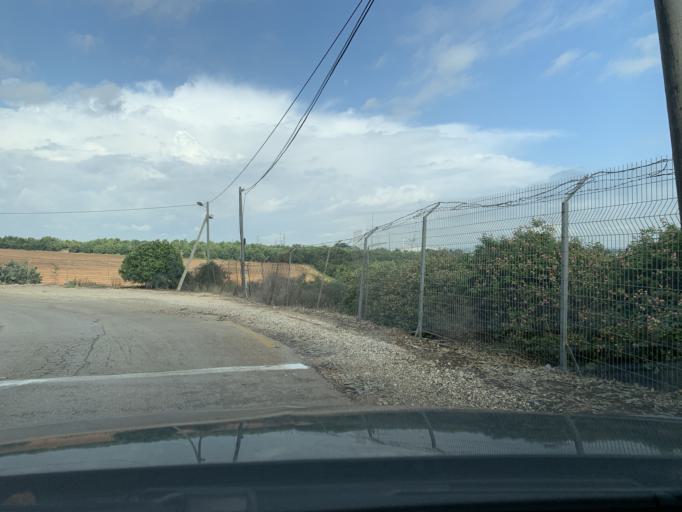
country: PS
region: West Bank
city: Qalqilyah
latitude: 32.1966
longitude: 34.9534
